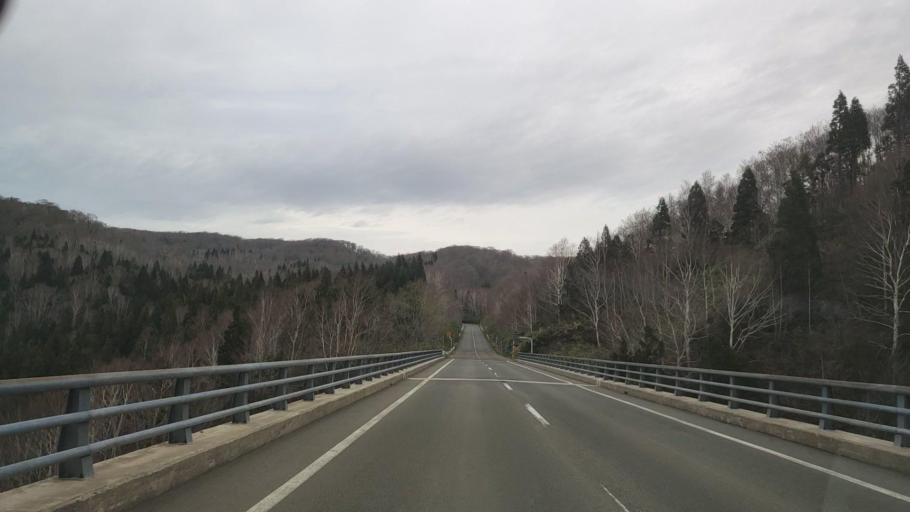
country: JP
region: Akita
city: Hanawa
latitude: 40.4133
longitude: 140.8462
